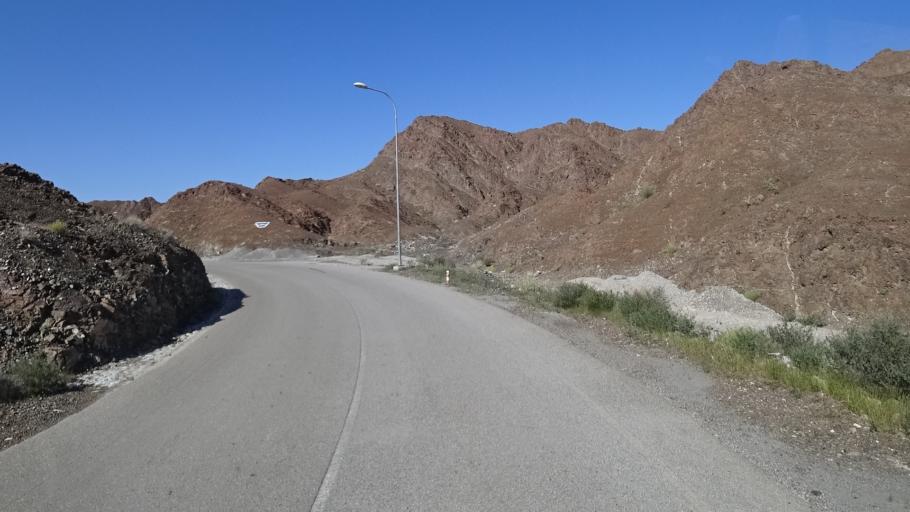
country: OM
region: Al Batinah
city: Bayt al `Awabi
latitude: 23.3645
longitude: 57.6704
